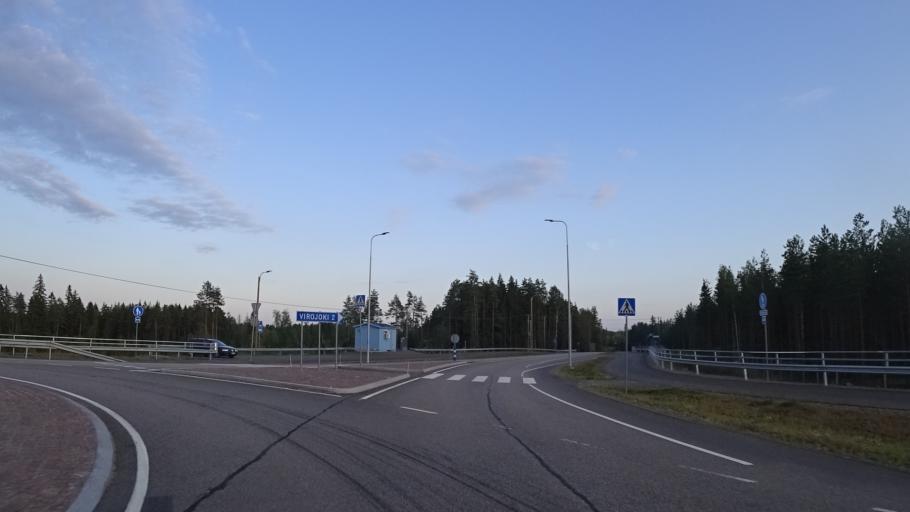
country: FI
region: Kymenlaakso
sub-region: Kotka-Hamina
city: Virojoki
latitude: 60.6044
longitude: 27.7036
